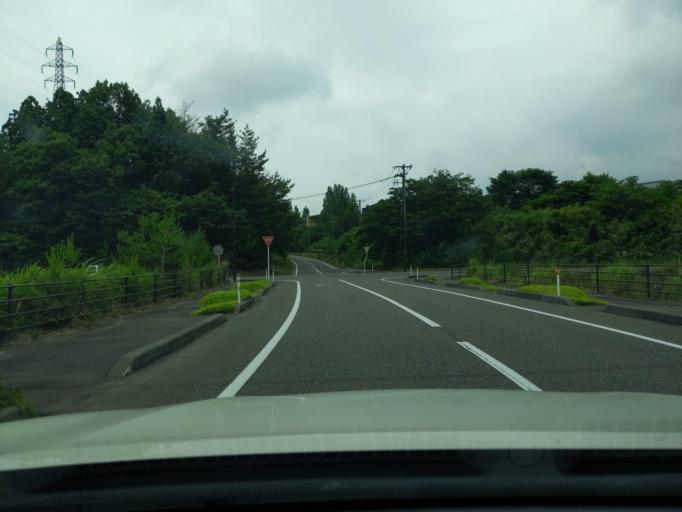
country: JP
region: Niigata
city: Kashiwazaki
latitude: 37.3411
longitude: 138.5938
